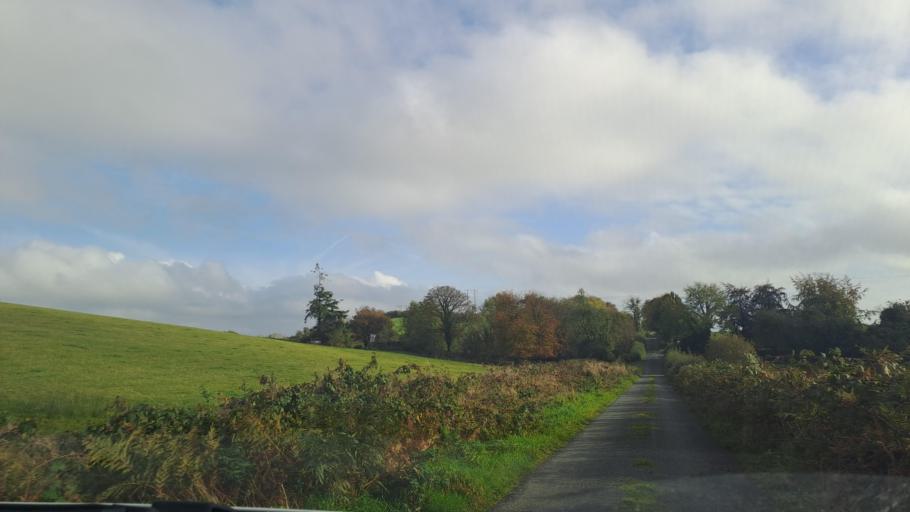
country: IE
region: Ulster
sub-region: County Monaghan
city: Carrickmacross
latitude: 54.0215
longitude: -6.7656
